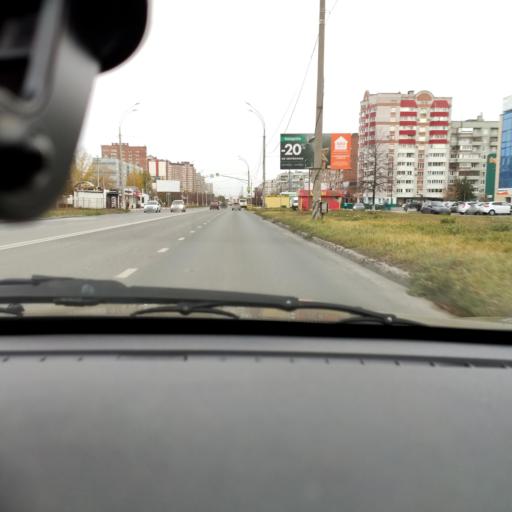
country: RU
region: Samara
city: Tol'yatti
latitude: 53.5416
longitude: 49.3398
